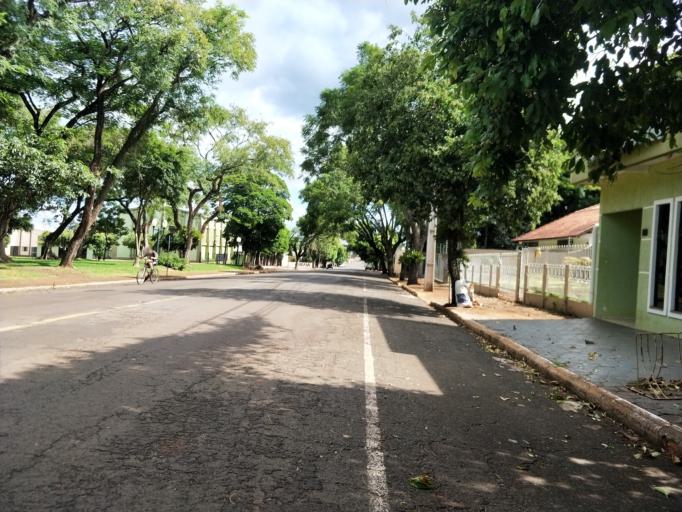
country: BR
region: Parana
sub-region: Marechal Candido Rondon
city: Marechal Candido Rondon
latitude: -24.5620
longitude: -54.0560
